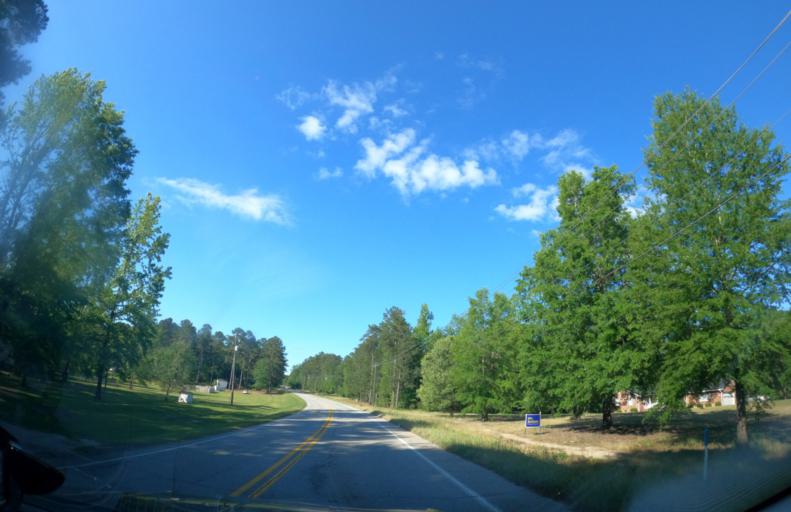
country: US
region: Georgia
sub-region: Columbia County
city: Grovetown
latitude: 33.4492
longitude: -82.2458
